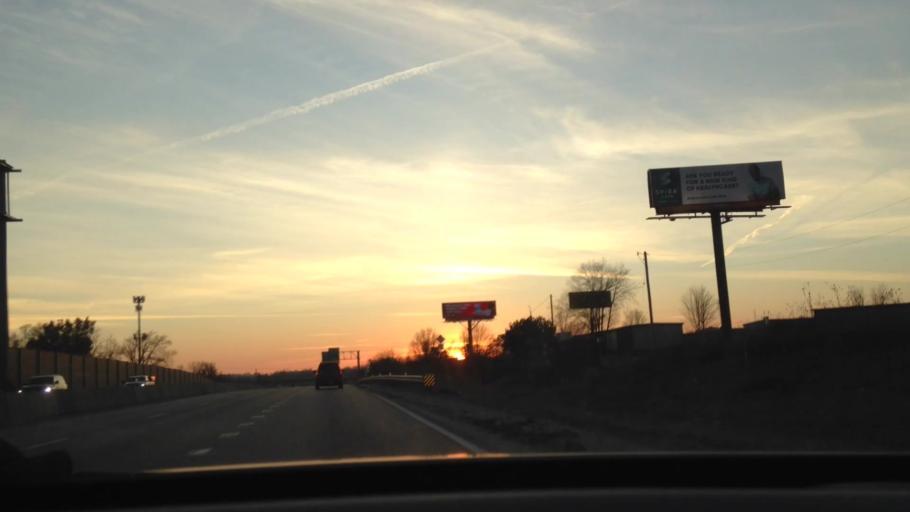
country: US
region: Missouri
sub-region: Clay County
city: Pleasant Valley
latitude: 39.2131
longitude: -94.4793
